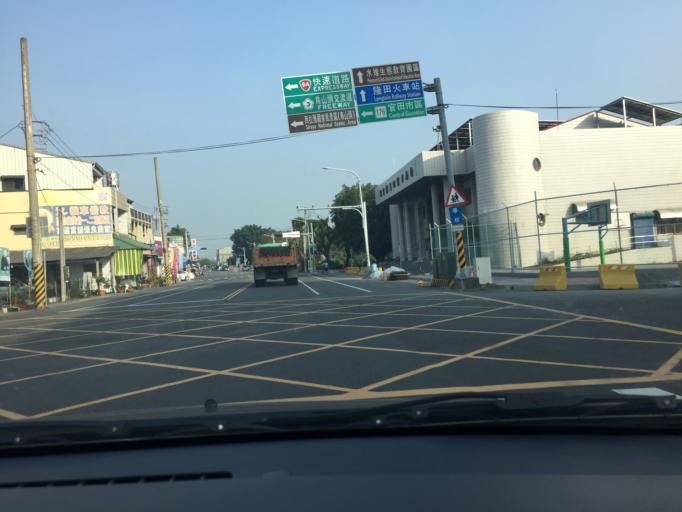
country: TW
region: Taiwan
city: Xinying
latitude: 23.1930
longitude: 120.3134
